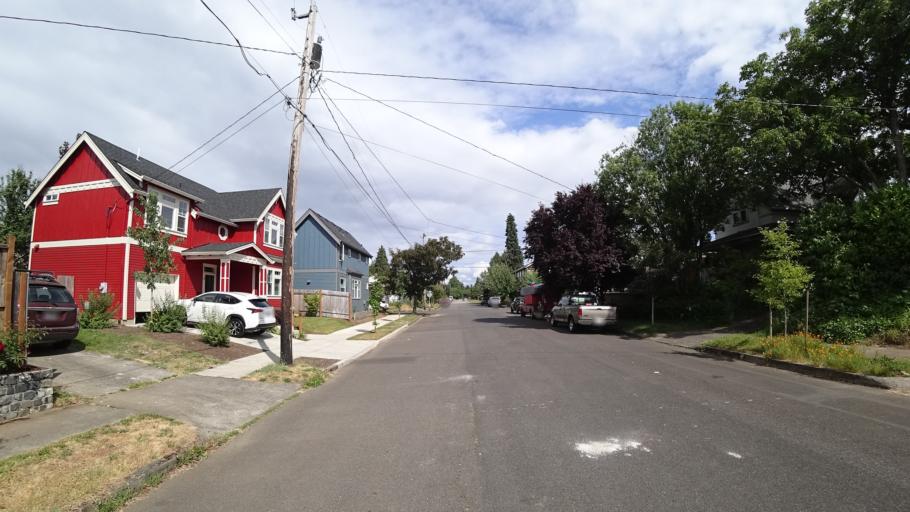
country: US
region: Oregon
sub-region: Washington County
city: West Haven
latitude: 45.5922
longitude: -122.7486
